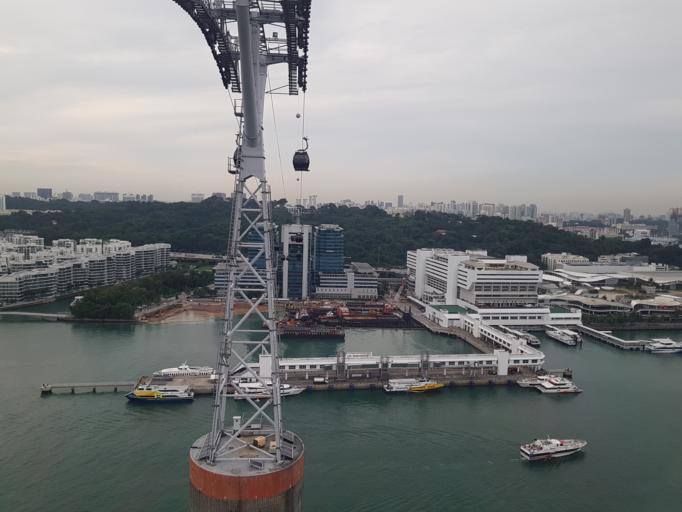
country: SG
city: Singapore
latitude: 1.2591
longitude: 103.8181
